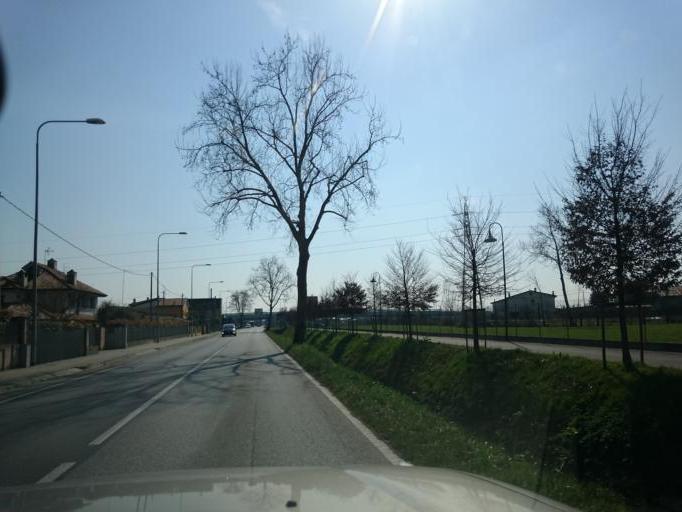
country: IT
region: Veneto
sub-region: Provincia di Padova
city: Albignasego
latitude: 45.3714
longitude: 11.8884
